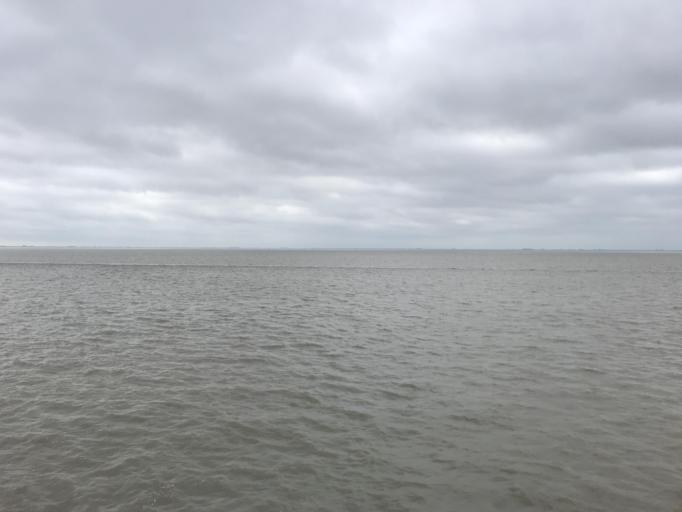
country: DE
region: Lower Saxony
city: Emden
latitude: 53.3309
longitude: 7.1346
